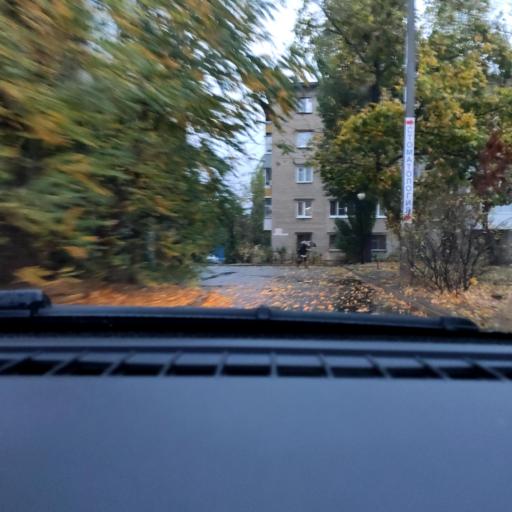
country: RU
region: Voronezj
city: Voronezh
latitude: 51.6890
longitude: 39.2660
